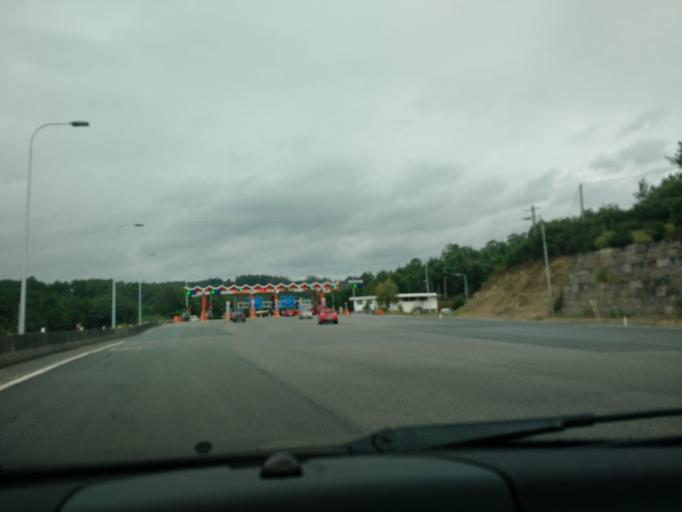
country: ES
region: Galicia
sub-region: Provincia da Coruna
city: Bergondo
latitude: 43.2823
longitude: -8.2727
